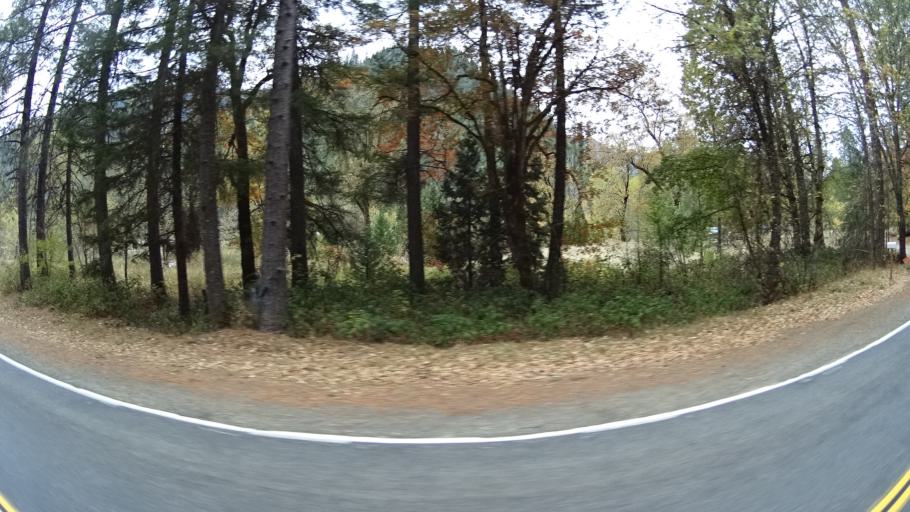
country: US
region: California
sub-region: Siskiyou County
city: Happy Camp
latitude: 41.8527
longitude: -123.3879
